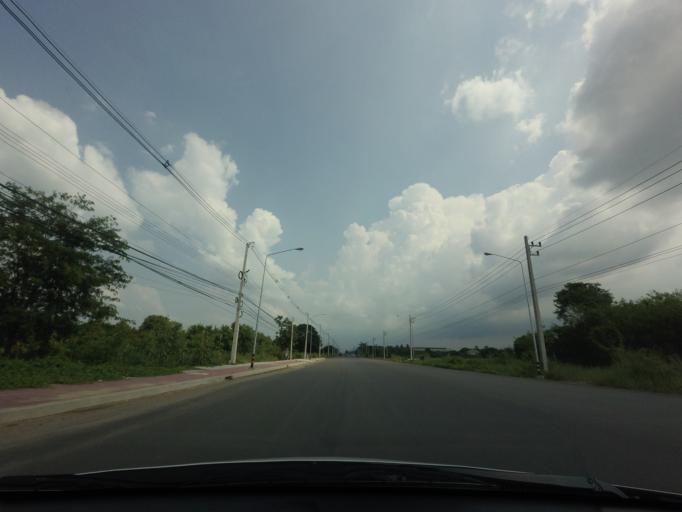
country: TH
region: Nakhon Pathom
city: Nakhon Chai Si
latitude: 13.8042
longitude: 100.2068
